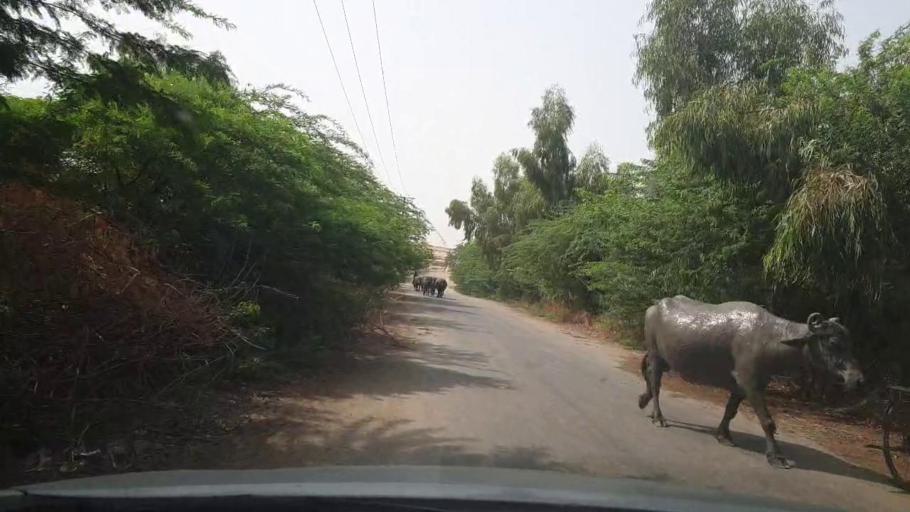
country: PK
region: Sindh
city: Kot Diji
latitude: 27.3485
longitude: 68.7126
